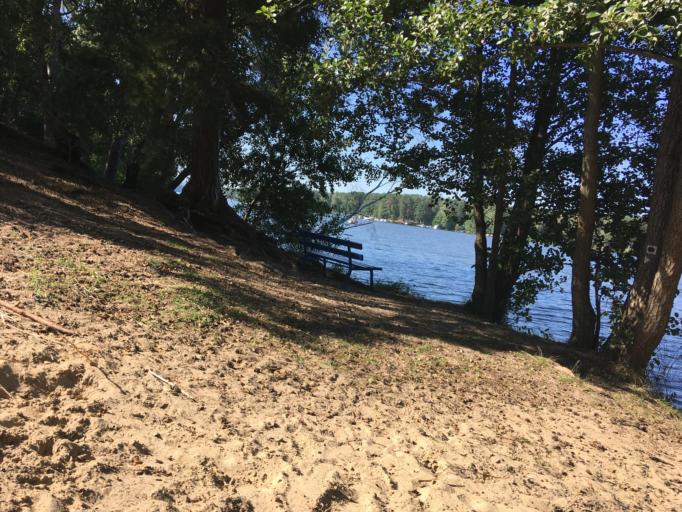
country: DE
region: Brandenburg
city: Gross Koris
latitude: 52.2141
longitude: 13.7533
